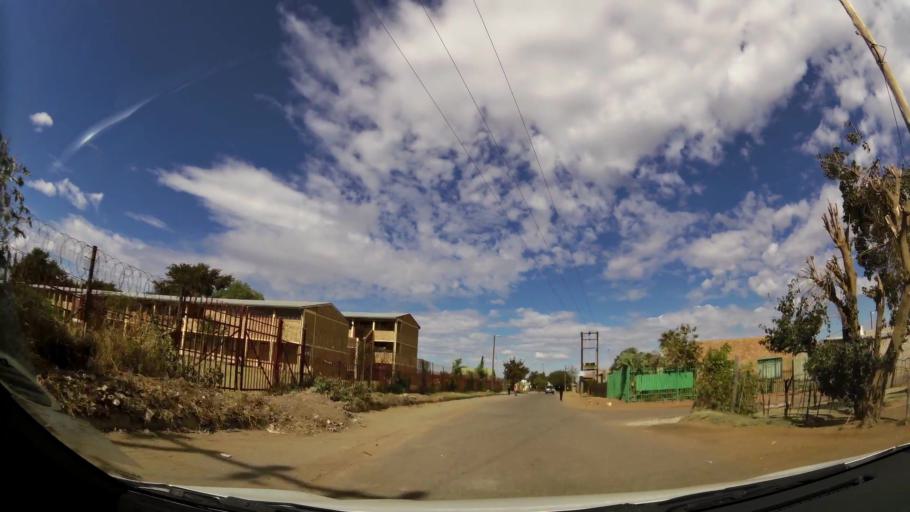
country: ZA
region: Limpopo
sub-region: Waterberg District Municipality
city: Bela-Bela
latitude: -24.8848
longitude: 28.3171
